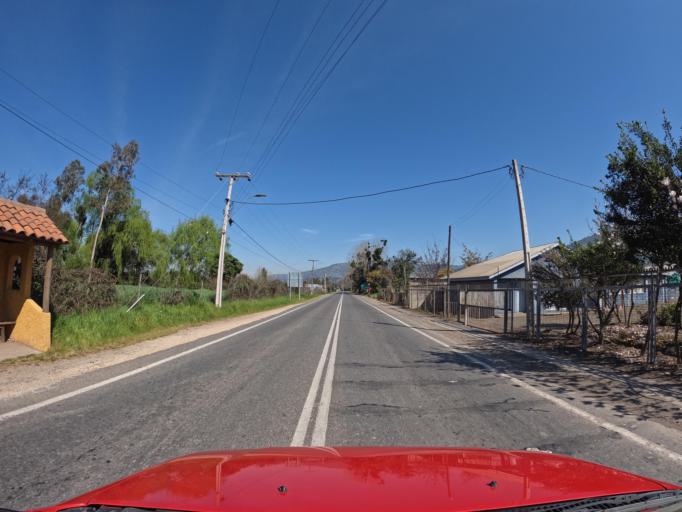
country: CL
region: Maule
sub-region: Provincia de Curico
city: Rauco
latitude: -34.9793
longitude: -71.4007
